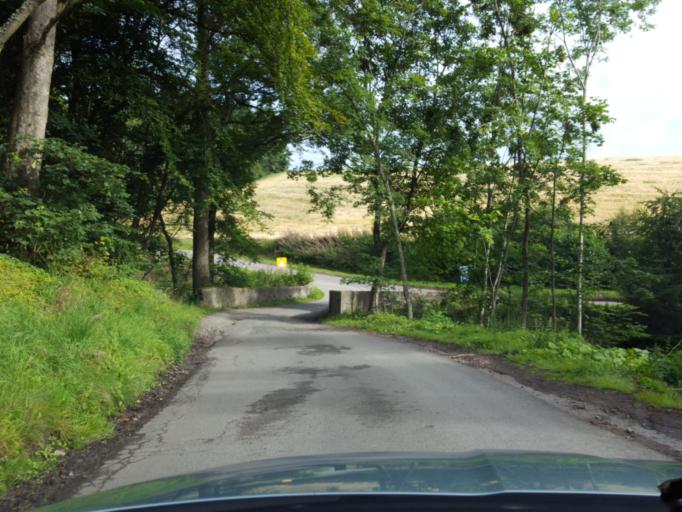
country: GB
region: Scotland
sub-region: Moray
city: Rothes
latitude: 57.4759
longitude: -3.1969
